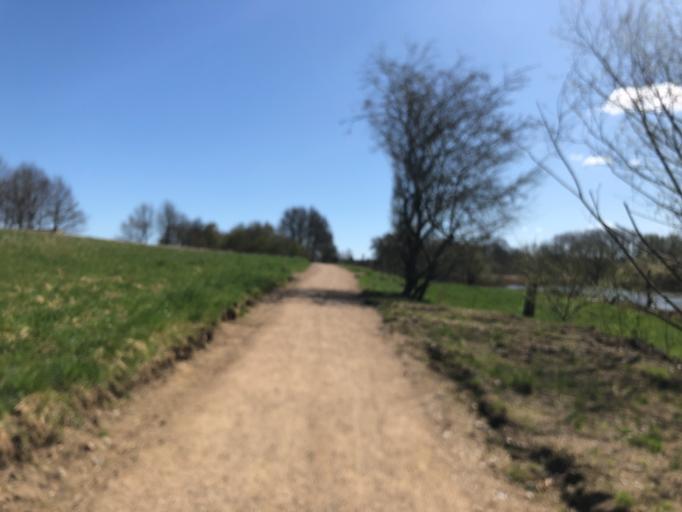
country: DK
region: Zealand
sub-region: Ringsted Kommune
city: Ringsted
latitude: 55.4218
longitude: 11.7763
